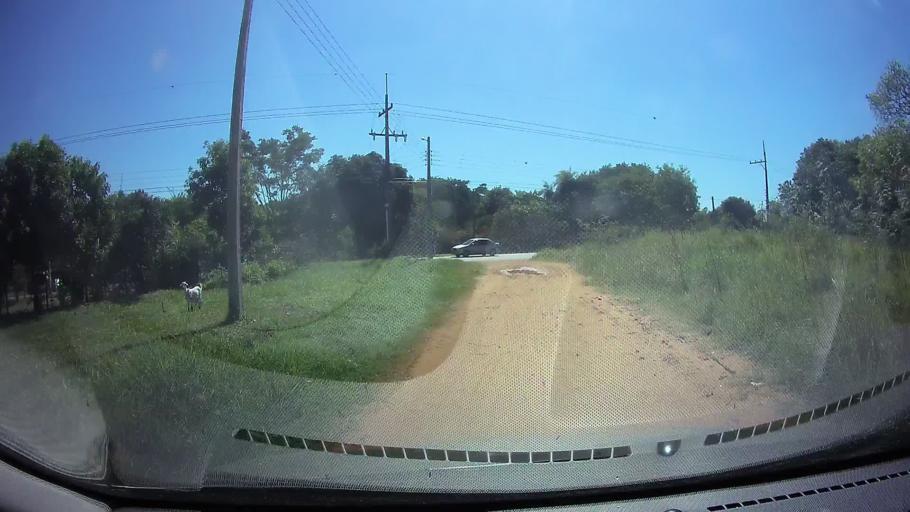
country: PY
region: Central
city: Limpio
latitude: -25.2361
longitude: -57.4494
